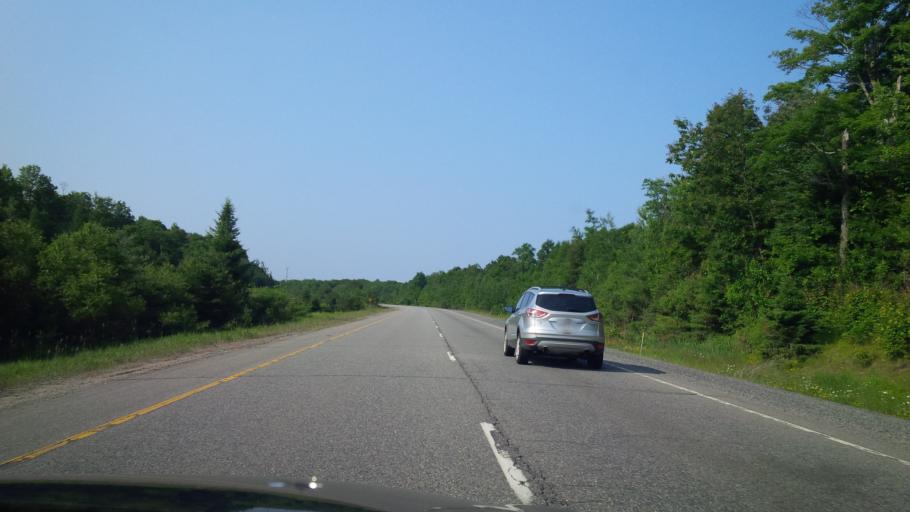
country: CA
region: Ontario
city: Huntsville
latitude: 45.2266
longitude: -79.3101
